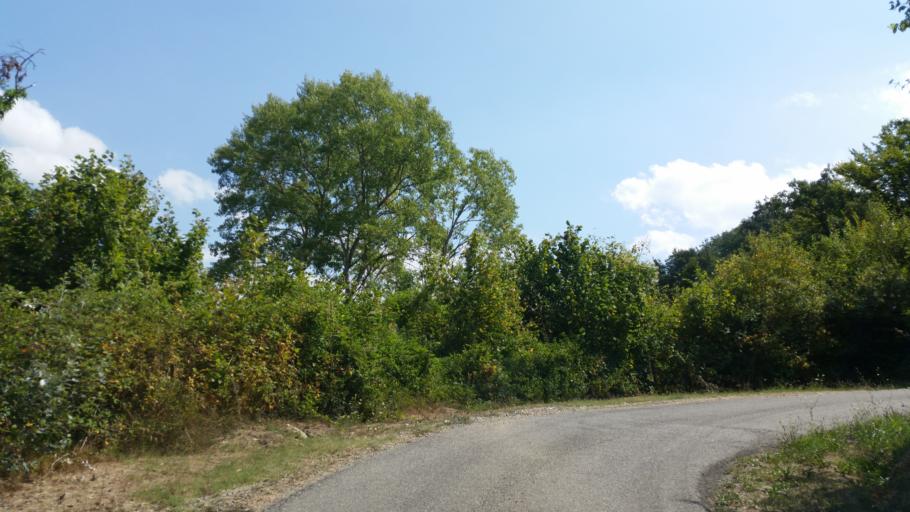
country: IT
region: Piedmont
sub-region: Provincia di Asti
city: Bubbio
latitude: 44.6335
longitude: 8.2946
